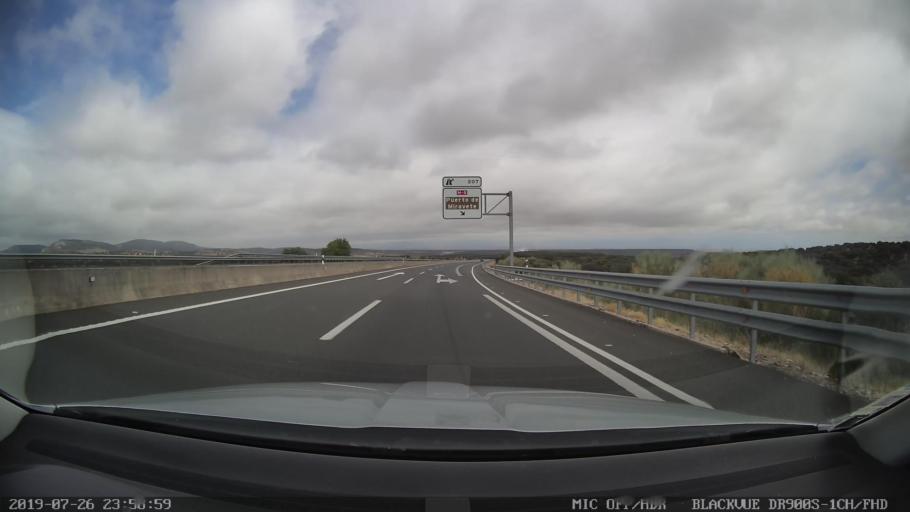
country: ES
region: Extremadura
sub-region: Provincia de Caceres
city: Casas de Miravete
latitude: 39.7594
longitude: -5.7325
